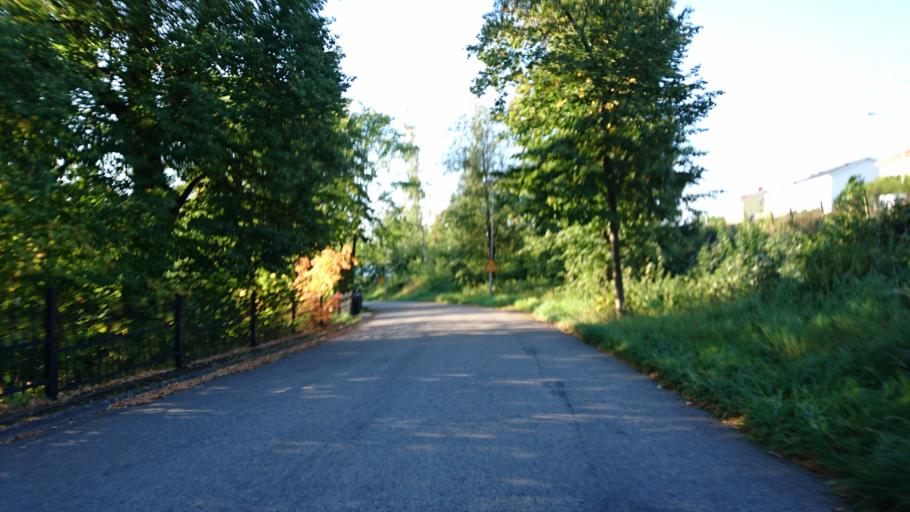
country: SE
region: Joenkoeping
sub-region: Jonkopings Kommun
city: Jonkoping
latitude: 57.8006
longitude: 14.1504
